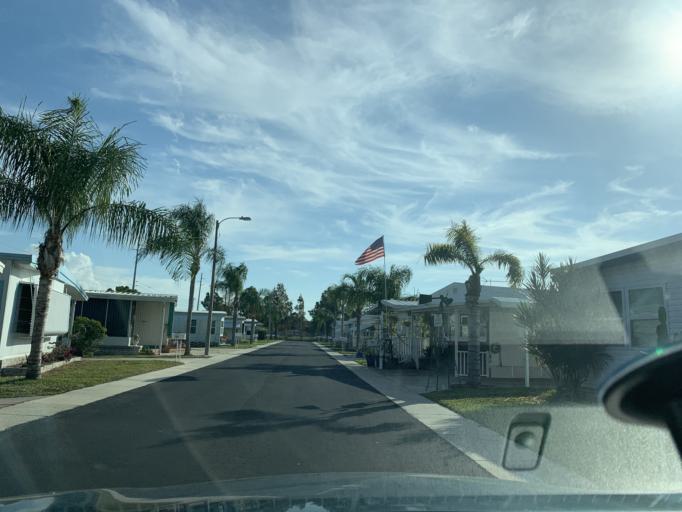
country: US
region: Florida
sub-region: Pinellas County
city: Largo
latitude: 27.8995
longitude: -82.7835
